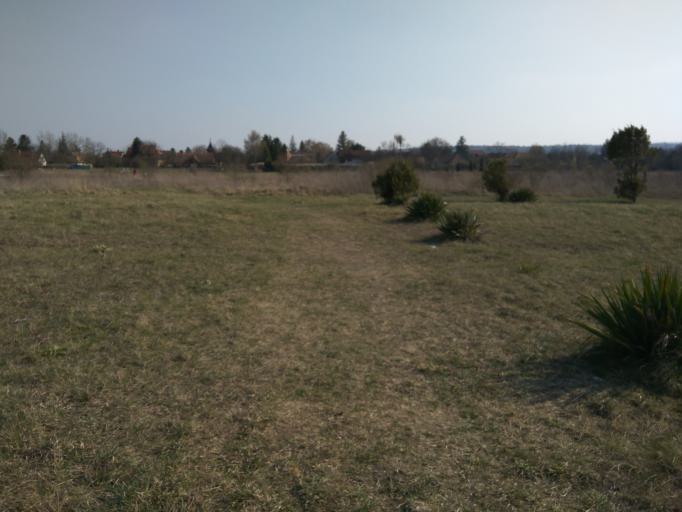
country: HU
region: Pest
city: Budakalasz
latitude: 47.6345
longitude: 19.0498
